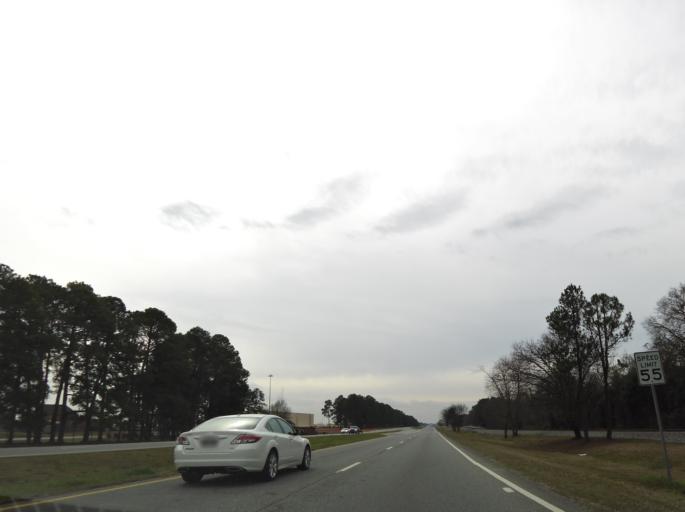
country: US
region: Georgia
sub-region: Houston County
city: Warner Robins
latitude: 32.6465
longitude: -83.6085
